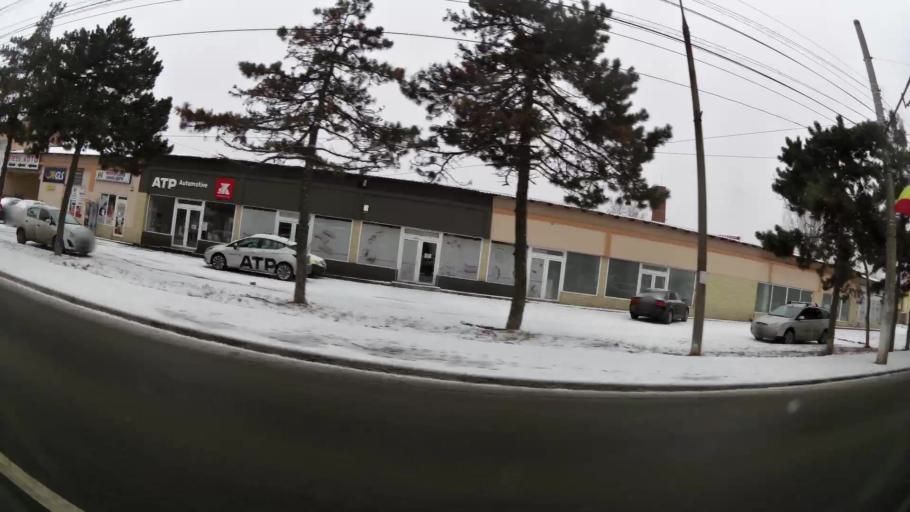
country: RO
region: Dambovita
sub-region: Municipiul Targoviste
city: Targoviste
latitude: 44.9144
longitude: 25.4510
